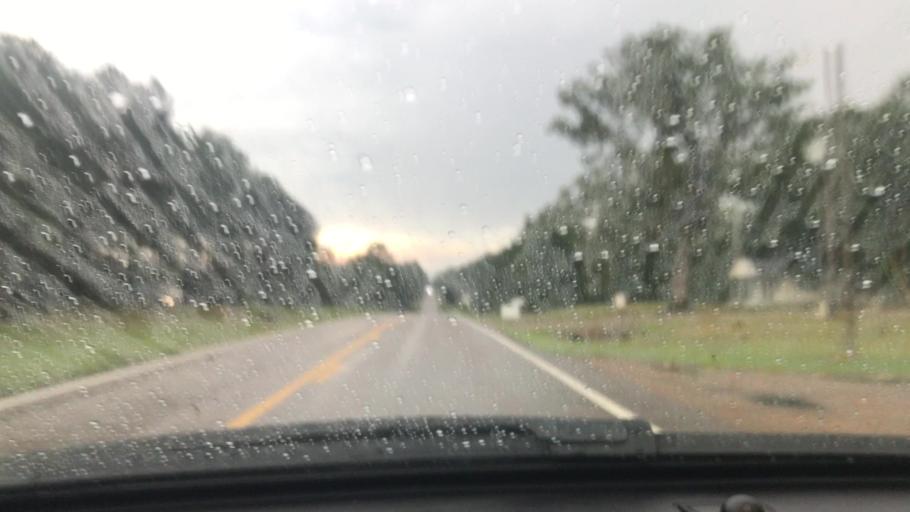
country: US
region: Mississippi
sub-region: Pike County
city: Summit
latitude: 31.3015
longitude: -90.5120
